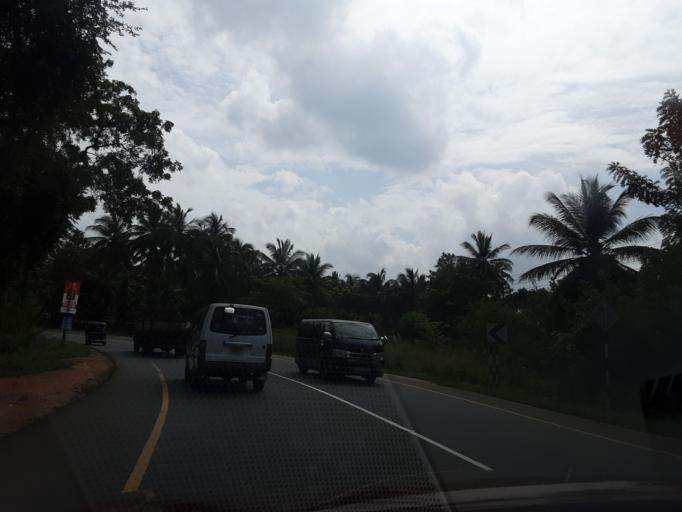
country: LK
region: North Central
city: Anuradhapura
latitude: 8.4813
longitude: 80.5097
